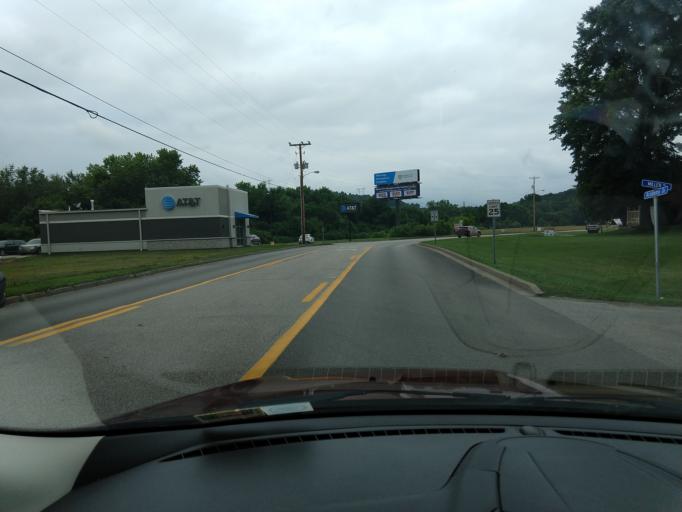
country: US
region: West Virginia
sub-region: Jackson County
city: Ripley
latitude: 38.8264
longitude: -81.7244
